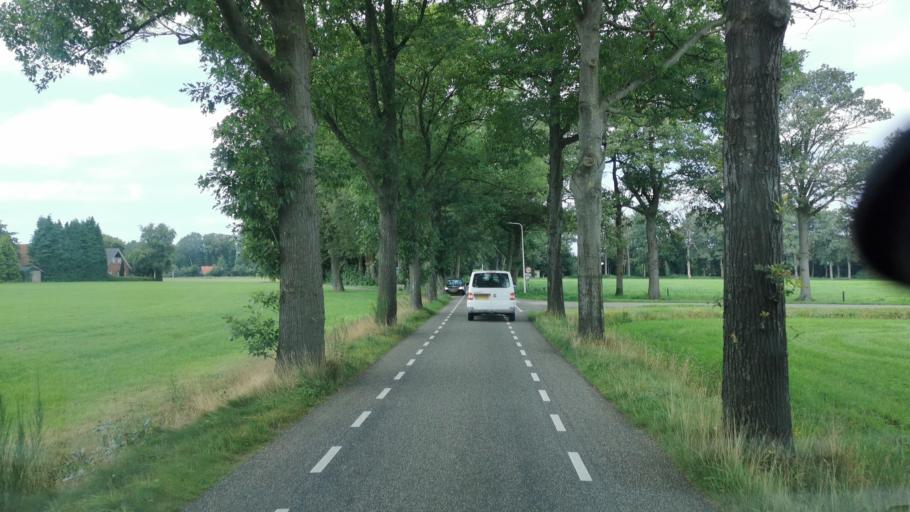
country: NL
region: Overijssel
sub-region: Gemeente Oldenzaal
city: Oldenzaal
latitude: 52.3215
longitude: 6.8618
